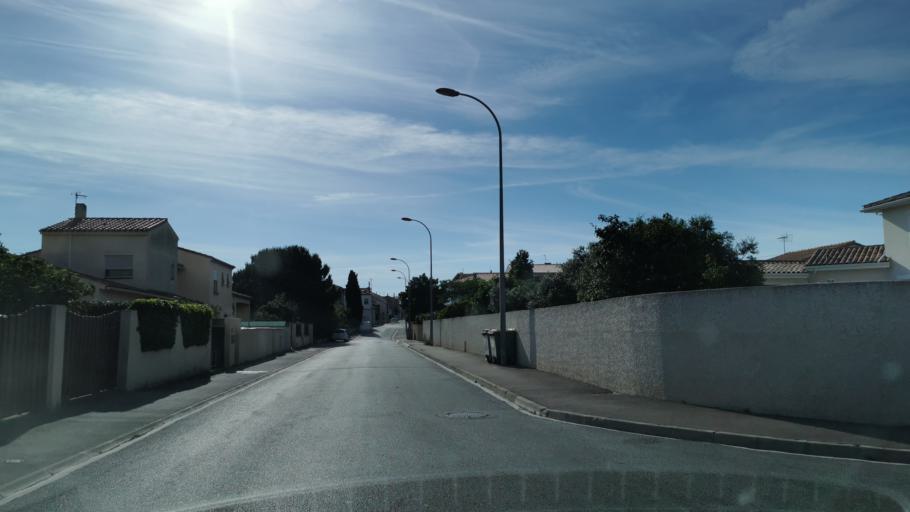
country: FR
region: Languedoc-Roussillon
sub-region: Departement de l'Aude
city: Narbonne
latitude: 43.1768
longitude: 3.0002
